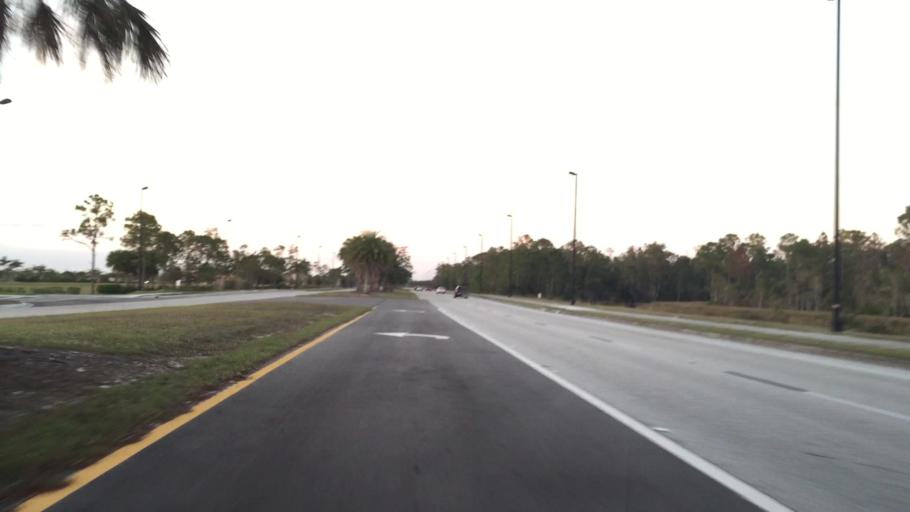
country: US
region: Florida
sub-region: Lee County
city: Three Oaks
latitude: 26.5292
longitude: -81.7856
